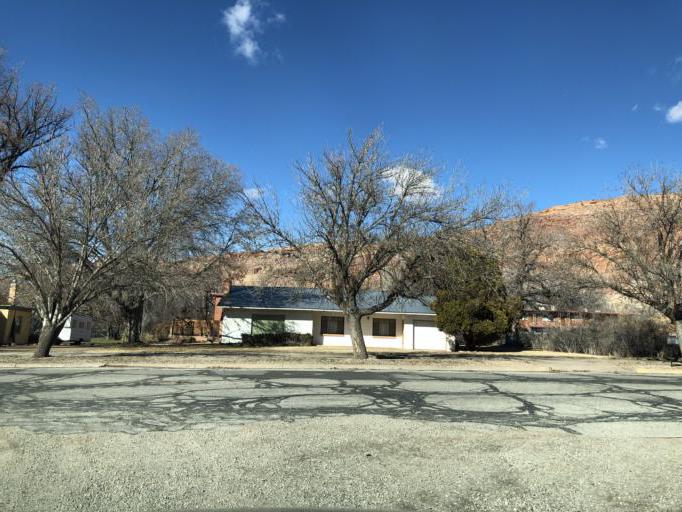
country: US
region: Utah
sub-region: Grand County
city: Moab
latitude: 38.5762
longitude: -109.5488
